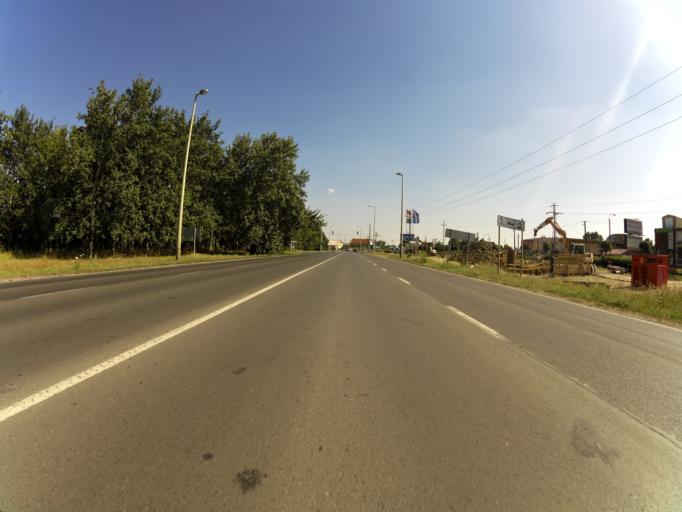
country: HU
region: Csongrad
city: Szeged
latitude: 46.2699
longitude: 20.1030
